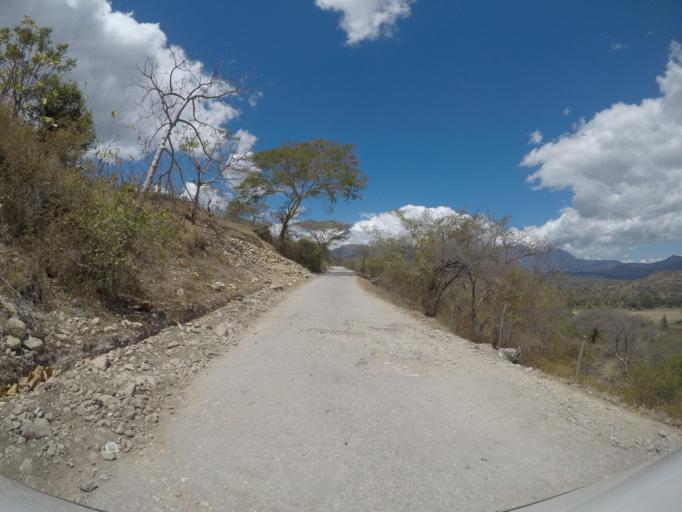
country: TL
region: Baucau
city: Baucau
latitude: -8.4834
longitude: 126.6089
